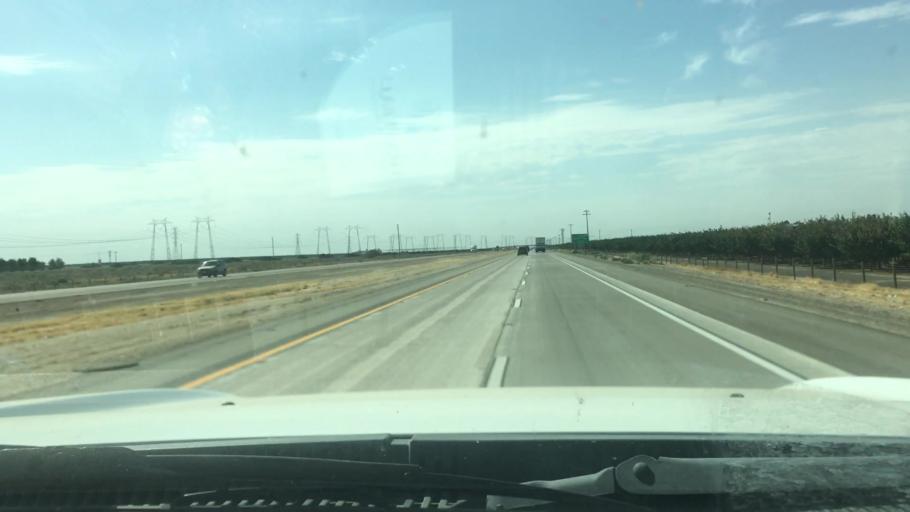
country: US
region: California
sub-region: Kern County
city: Buttonwillow
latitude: 35.5157
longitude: -119.5521
